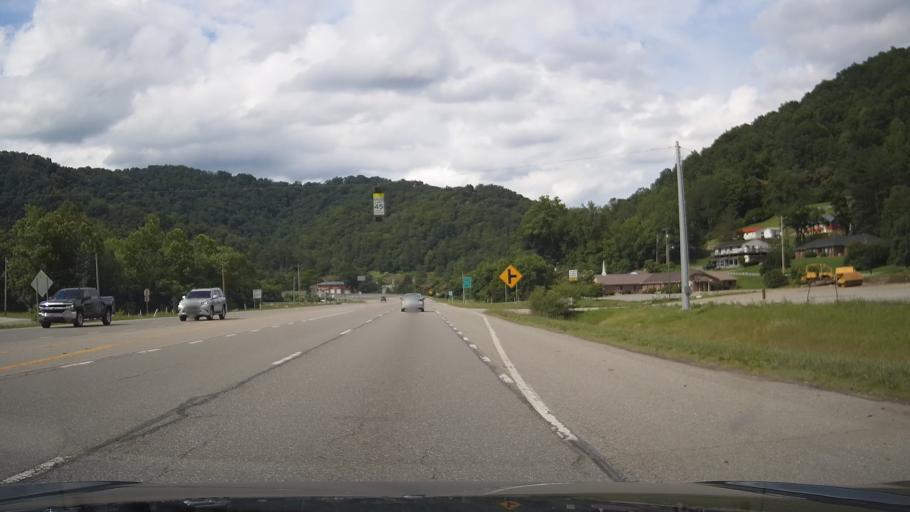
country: US
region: Kentucky
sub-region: Pike County
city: Coal Run Village
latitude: 37.5509
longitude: -82.6322
